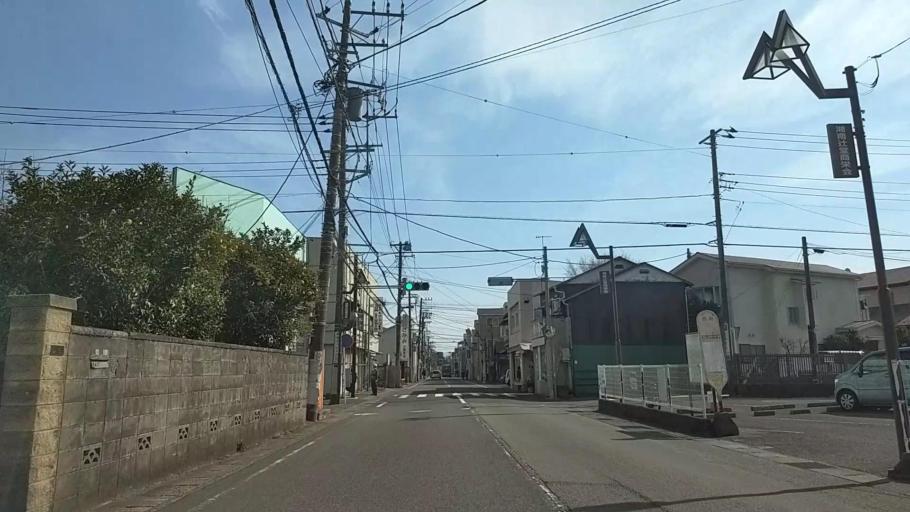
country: JP
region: Kanagawa
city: Fujisawa
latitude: 35.3322
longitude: 139.4508
